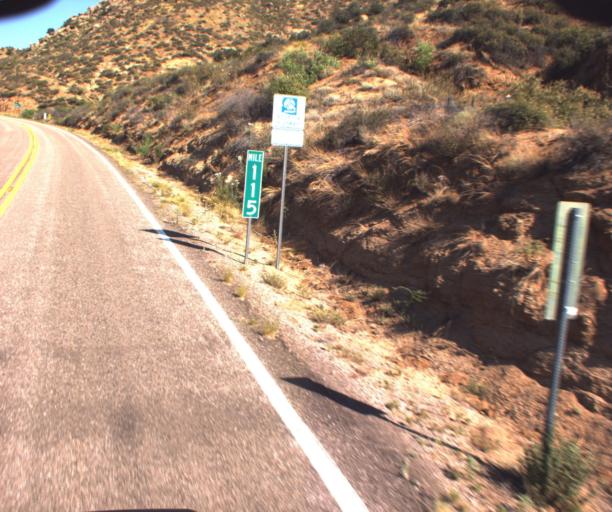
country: US
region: Arizona
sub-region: Graham County
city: Swift Trail Junction
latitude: 32.5760
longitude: -109.8413
